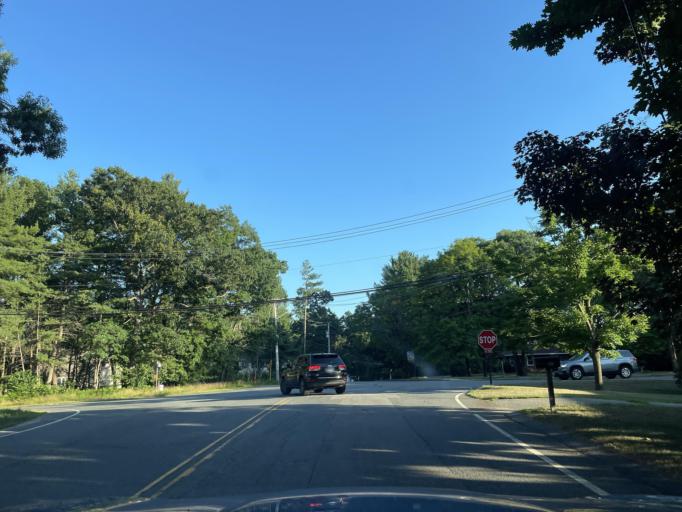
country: US
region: Massachusetts
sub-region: Plymouth County
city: Bridgewater
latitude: 42.0035
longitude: -70.9525
